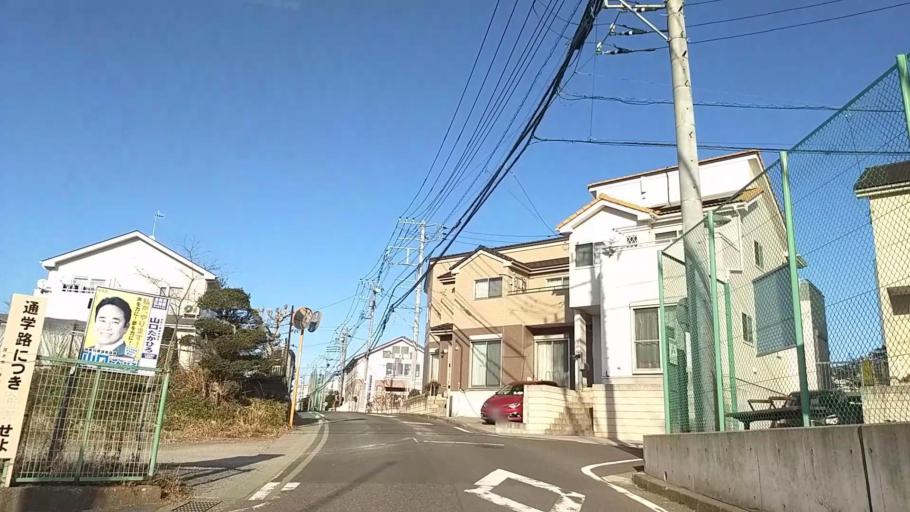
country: JP
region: Kanagawa
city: Atsugi
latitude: 35.4448
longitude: 139.3385
